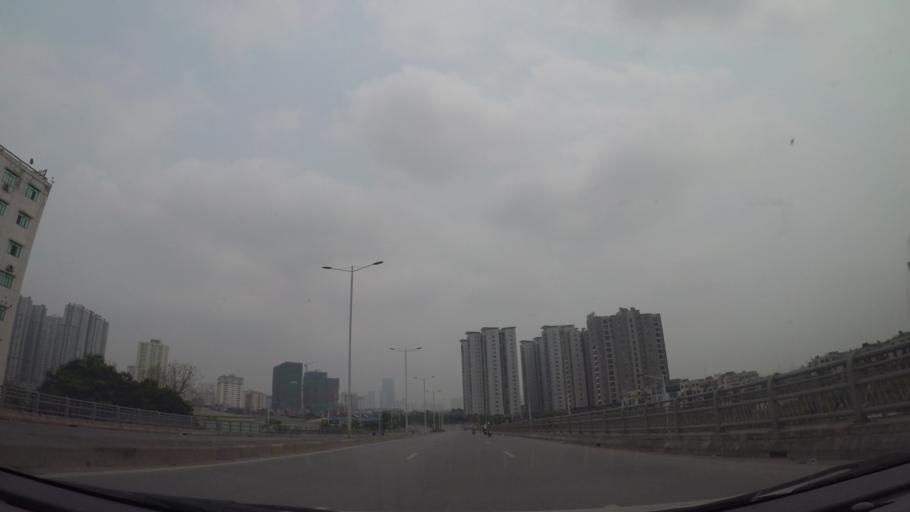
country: VN
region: Ha Noi
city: Cau Dien
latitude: 21.0337
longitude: 105.7531
